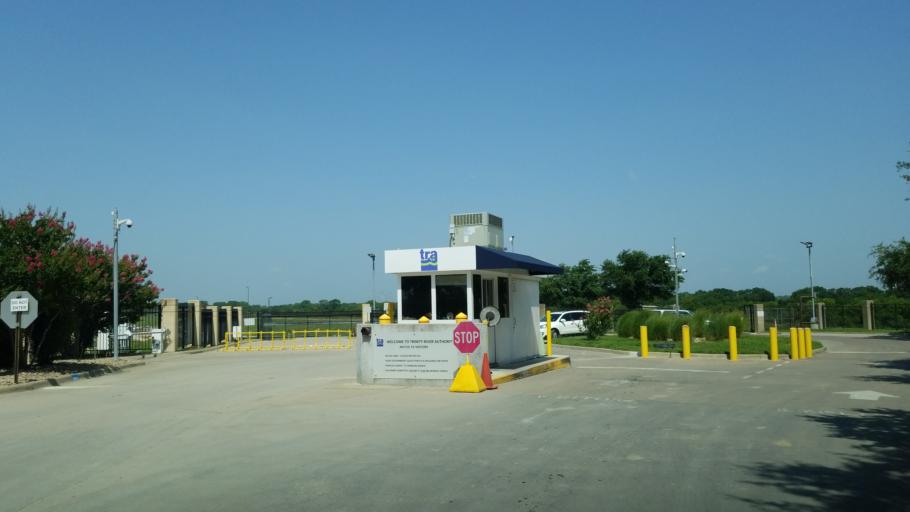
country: US
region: Texas
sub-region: Dallas County
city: Irving
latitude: 32.7788
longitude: -96.9281
